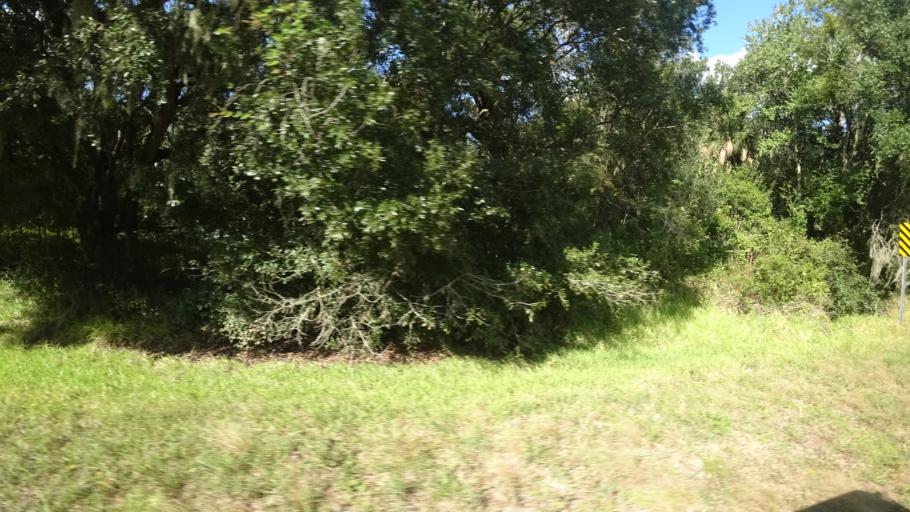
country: US
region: Florida
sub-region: DeSoto County
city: Nocatee
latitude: 27.2718
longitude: -82.0783
